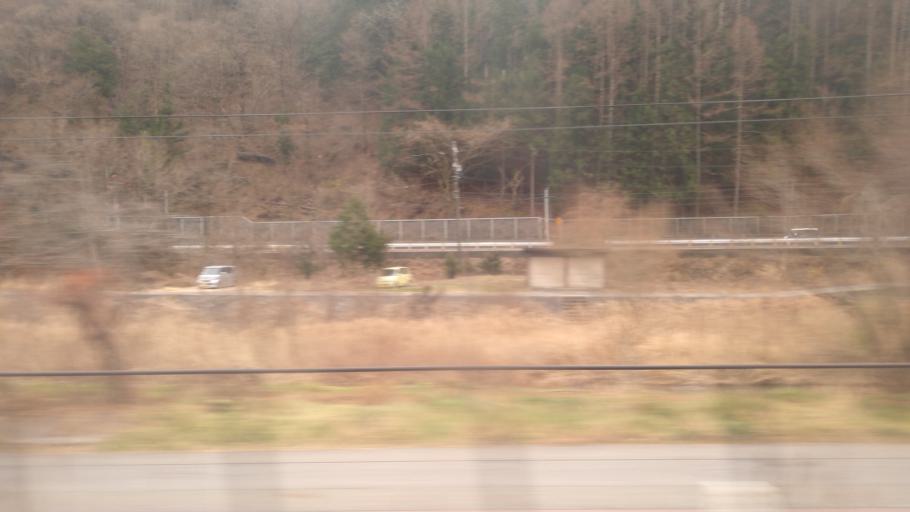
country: JP
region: Nagano
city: Tatsuno
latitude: 35.9650
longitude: 137.8117
